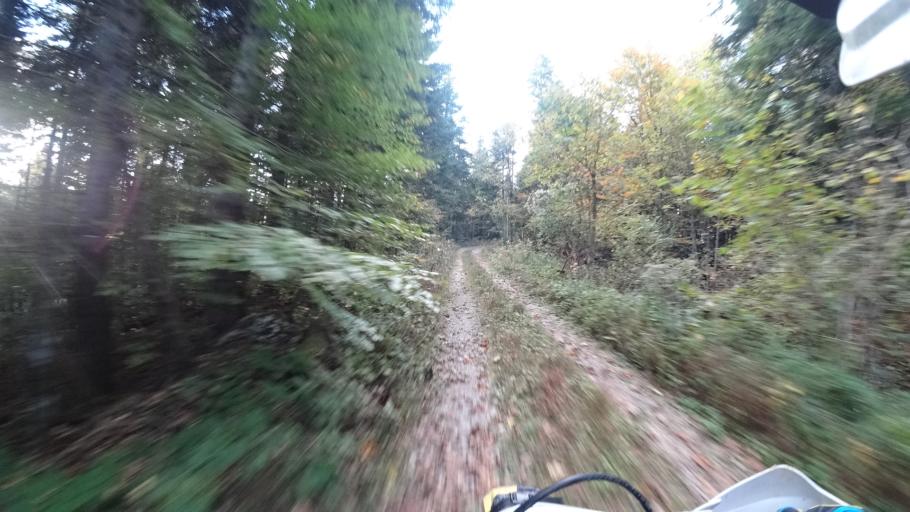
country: HR
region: Karlovacka
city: Plaski
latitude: 45.0185
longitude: 15.4343
